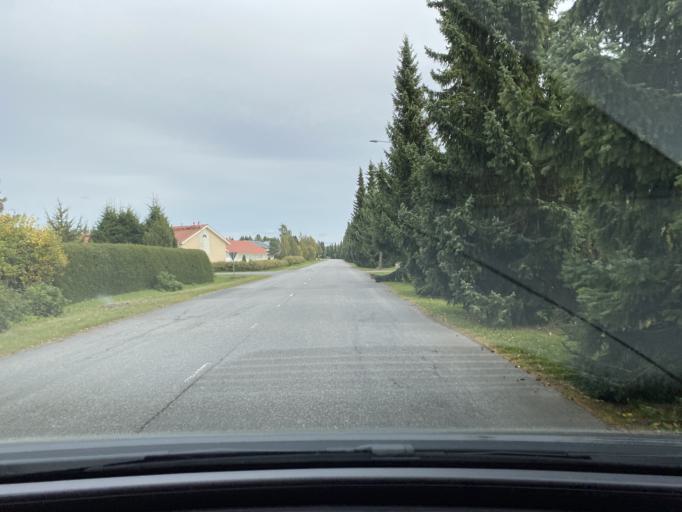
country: FI
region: Satakunta
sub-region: Pori
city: Huittinen
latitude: 61.1735
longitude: 22.7008
